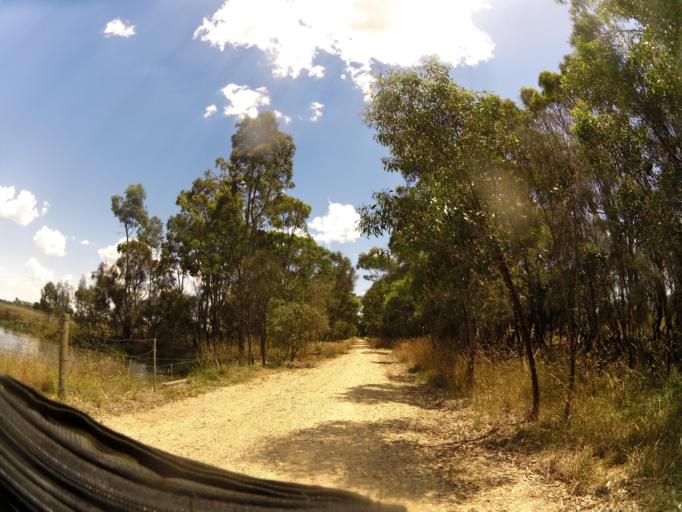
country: AU
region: Victoria
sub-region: Wellington
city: Heyfield
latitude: -37.9819
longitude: 146.8094
